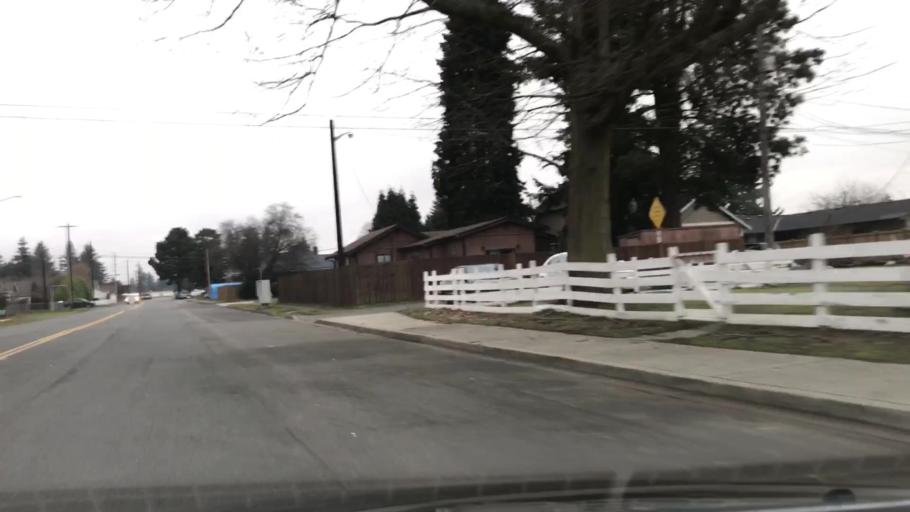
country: US
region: Washington
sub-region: Snohomish County
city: Marysville
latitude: 48.0520
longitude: -122.1696
